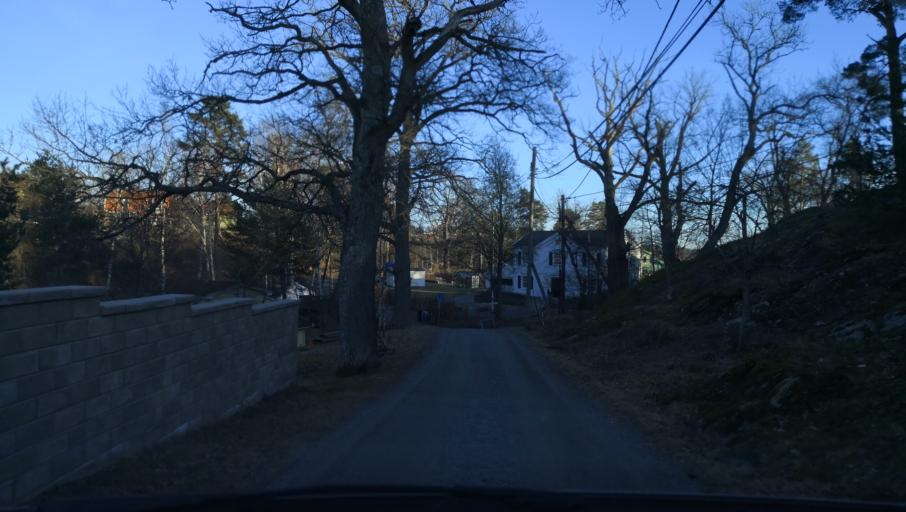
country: SE
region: Stockholm
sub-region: Varmdo Kommun
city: Mortnas
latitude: 59.3280
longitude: 18.4366
